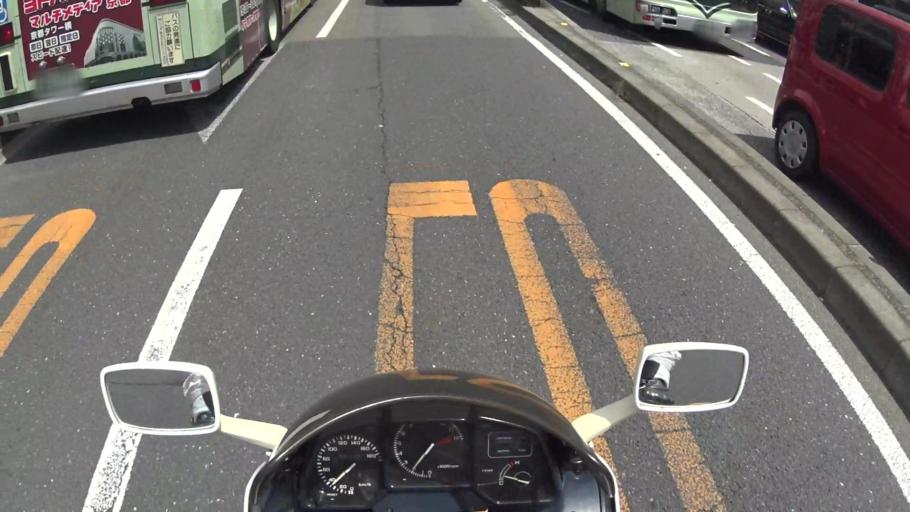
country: JP
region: Kyoto
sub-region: Kyoto-shi
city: Kamigyo-ku
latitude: 35.0415
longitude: 135.7384
